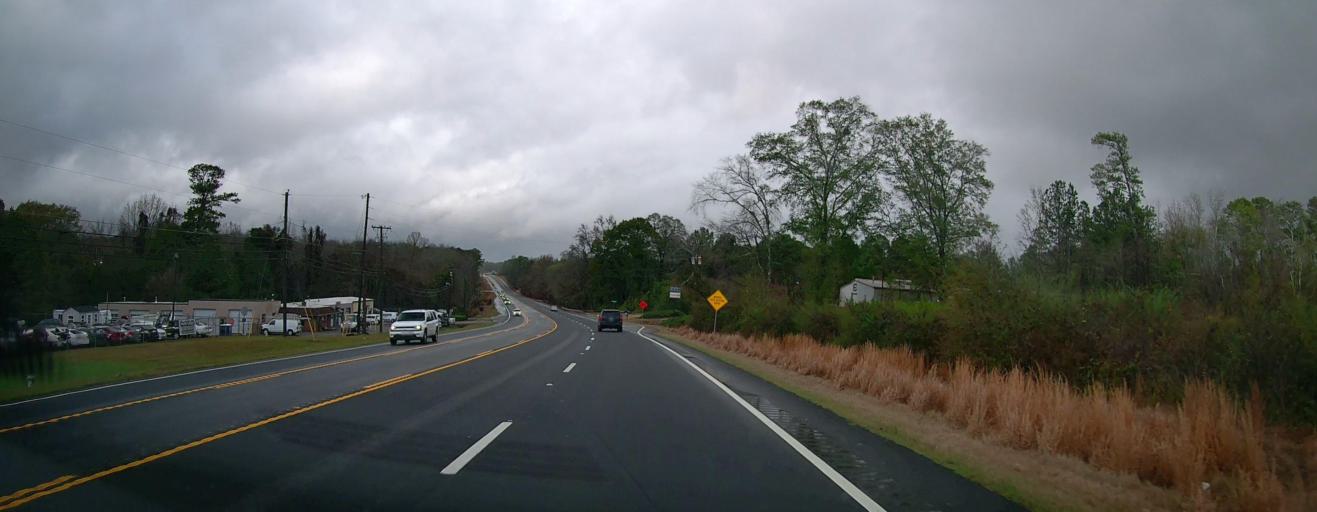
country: US
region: Georgia
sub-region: Clarke County
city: Athens
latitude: 33.9835
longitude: -83.3768
